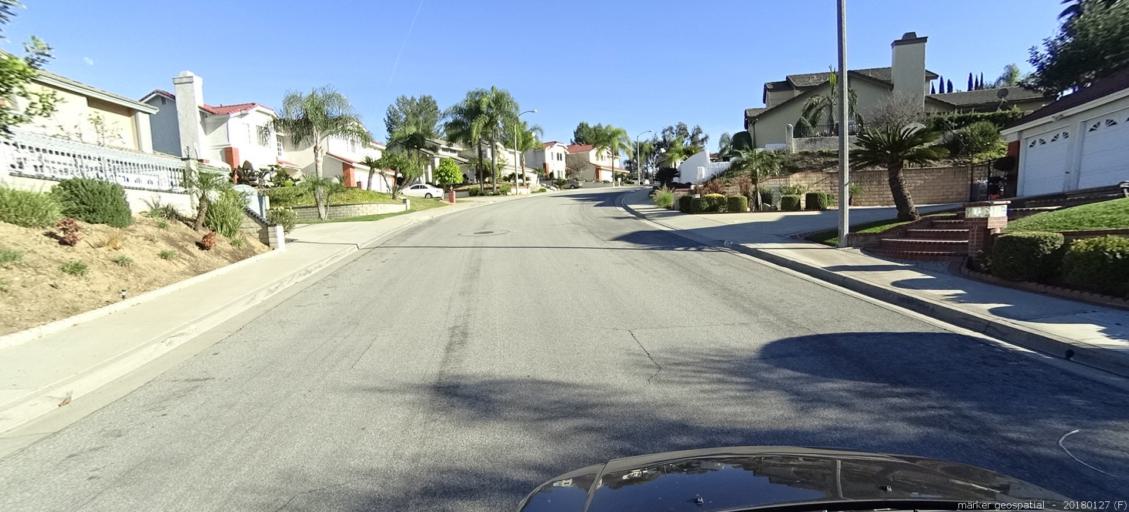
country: US
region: California
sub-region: Los Angeles County
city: Diamond Bar
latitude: 34.0159
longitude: -117.7942
